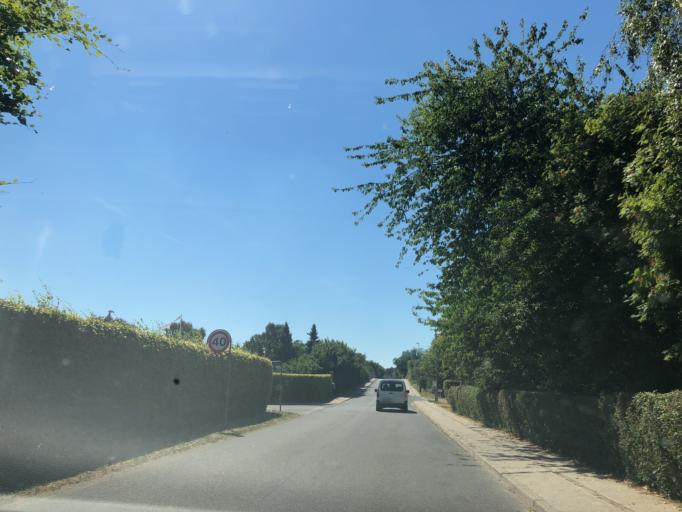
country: DK
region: Zealand
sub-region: Slagelse Kommune
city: Forlev
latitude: 55.3670
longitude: 11.2597
